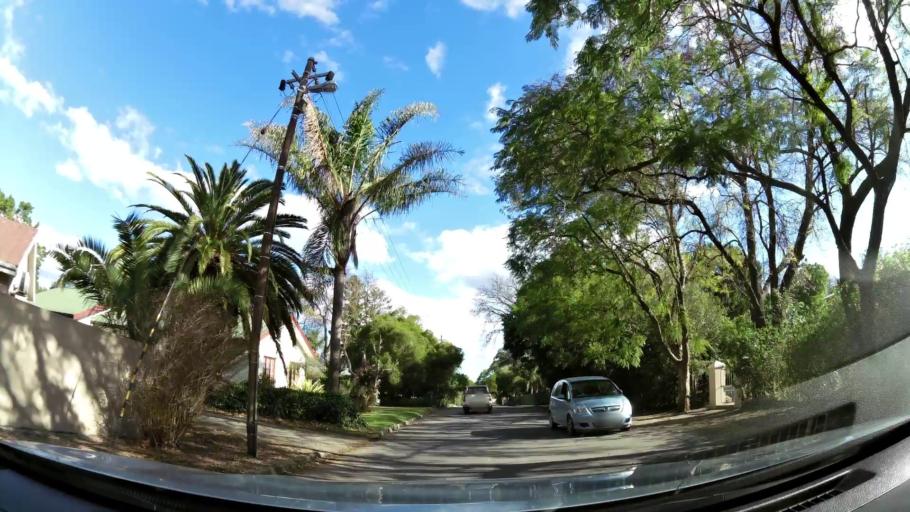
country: ZA
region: Western Cape
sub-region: Overberg District Municipality
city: Swellendam
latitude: -34.0237
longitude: 20.4430
